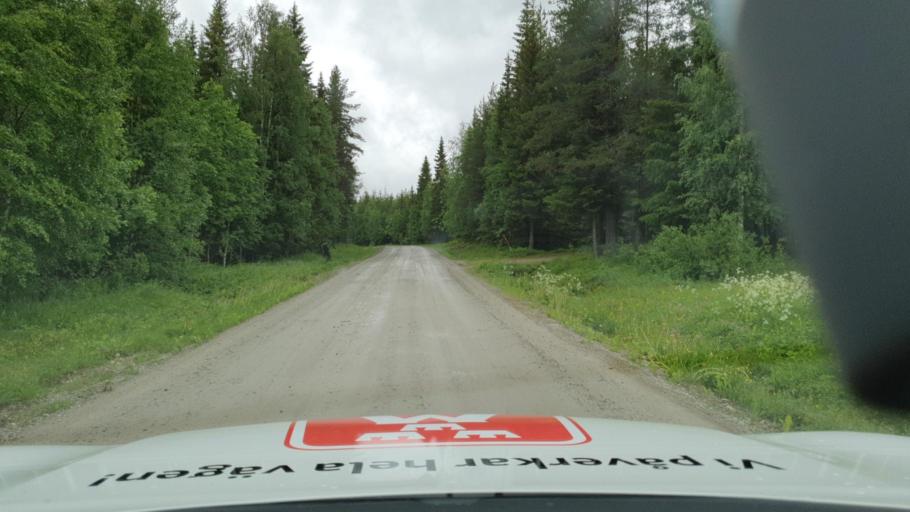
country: SE
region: Vaesterbotten
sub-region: Dorotea Kommun
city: Dorotea
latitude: 64.0268
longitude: 16.7888
